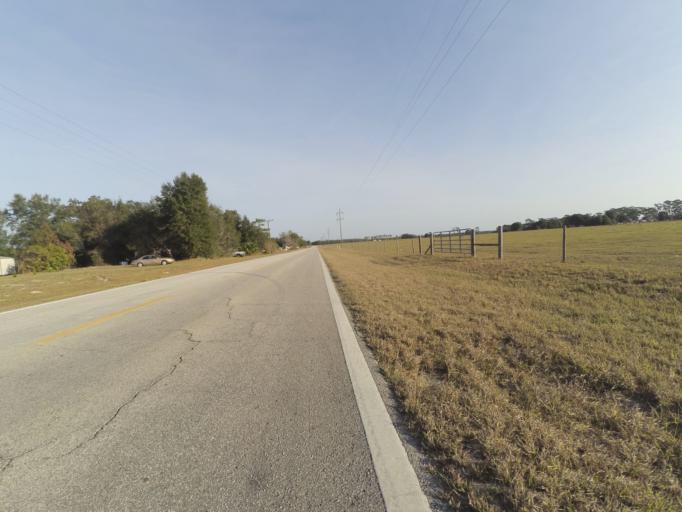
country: US
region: Florida
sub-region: Lake County
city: Umatilla
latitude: 28.9530
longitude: -81.6303
